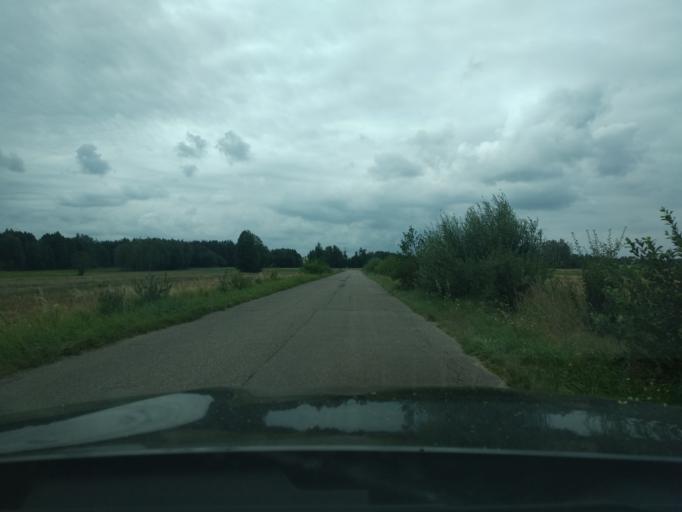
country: PL
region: Masovian Voivodeship
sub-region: Powiat pultuski
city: Obryte
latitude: 52.7469
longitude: 21.2155
